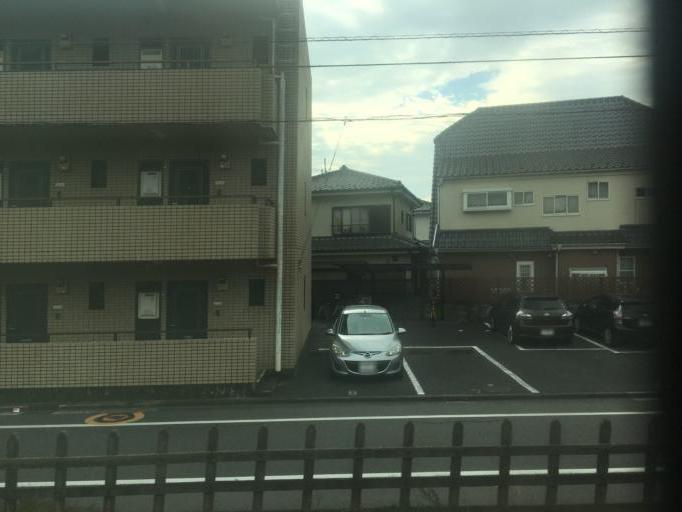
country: JP
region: Tokyo
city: Fussa
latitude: 35.7122
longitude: 139.3655
